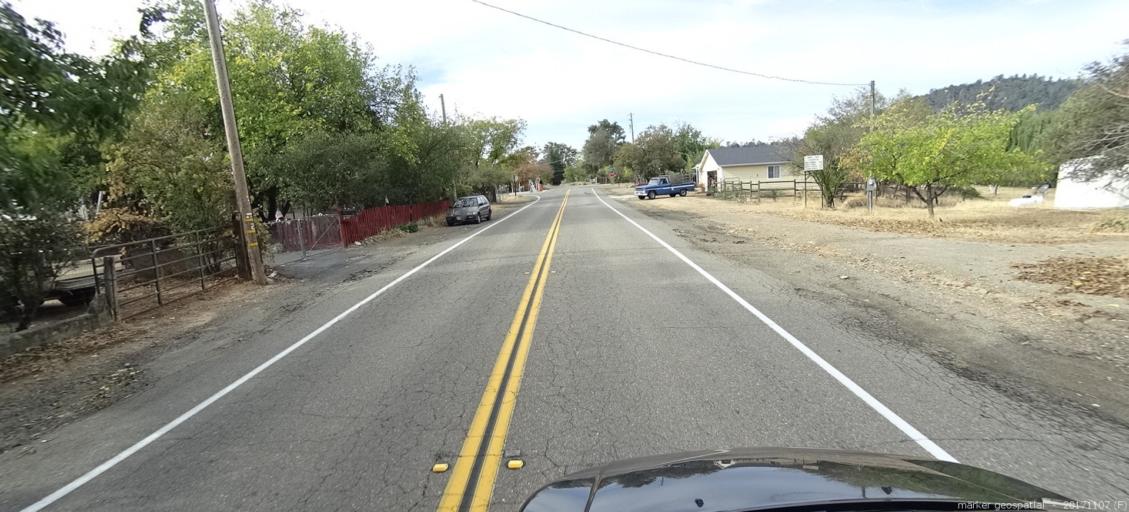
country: US
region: California
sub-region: Shasta County
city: Shasta
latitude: 40.5057
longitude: -122.5406
